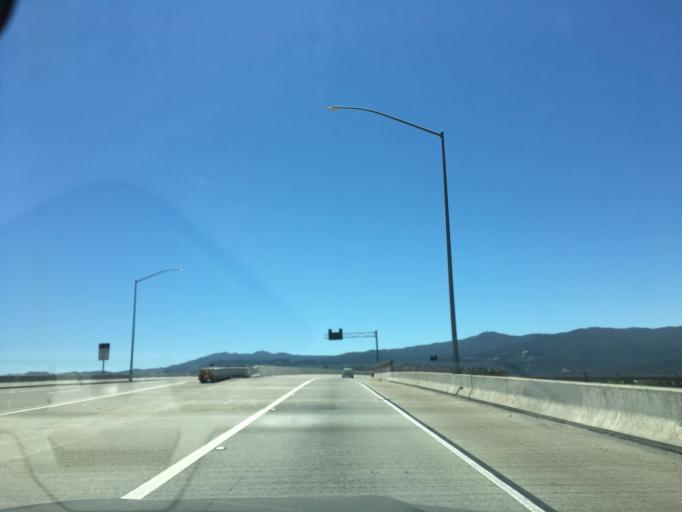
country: US
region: California
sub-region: Santa Clara County
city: Seven Trees
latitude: 37.2592
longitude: -121.8592
